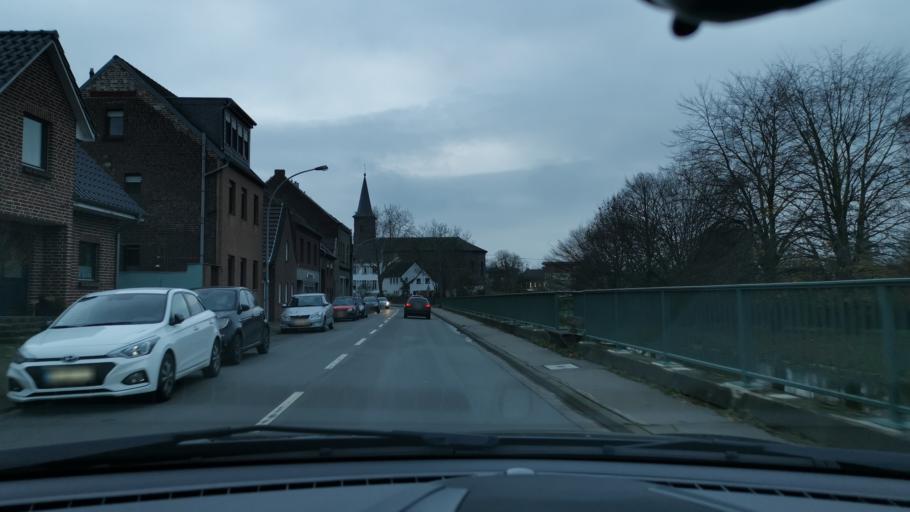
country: DE
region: North Rhine-Westphalia
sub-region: Regierungsbezirk Dusseldorf
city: Neubrueck
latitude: 51.1114
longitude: 6.6260
